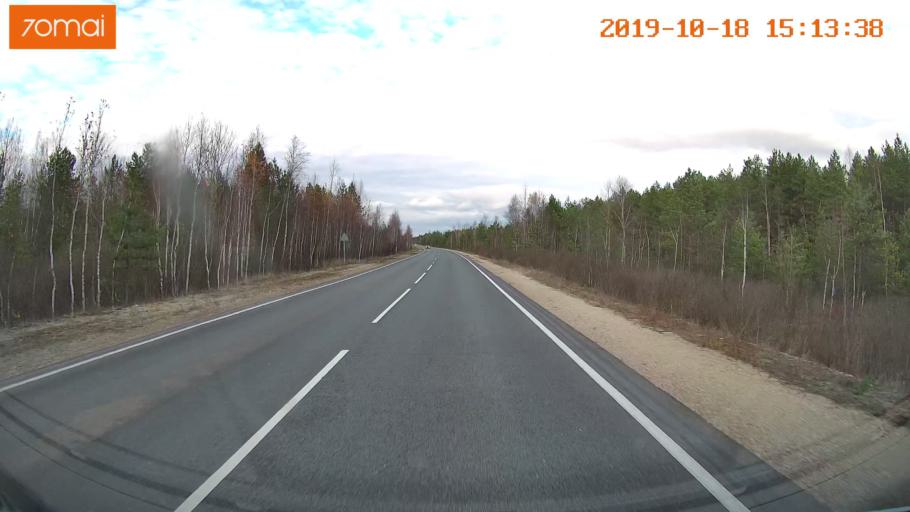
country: RU
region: Vladimir
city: Gus'-Khrustal'nyy
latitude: 55.5896
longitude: 40.7184
